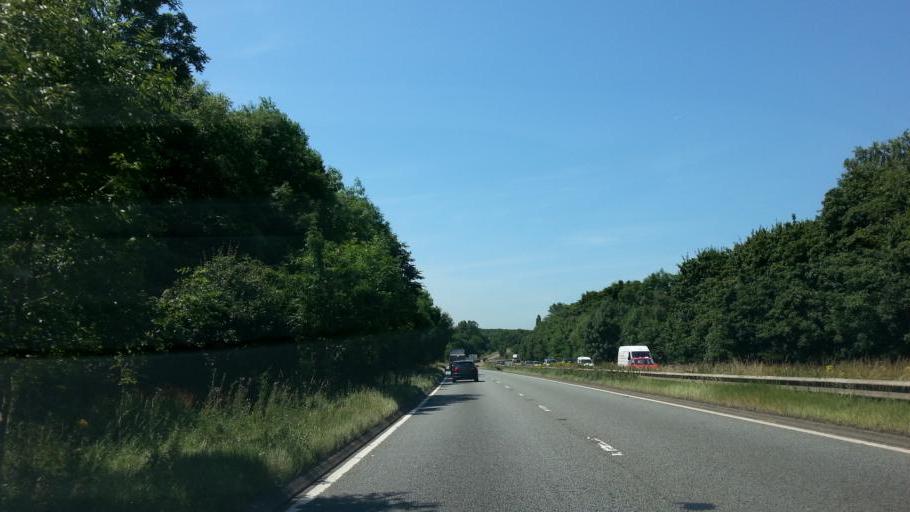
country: GB
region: England
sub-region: Derbyshire
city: Alfreton
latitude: 53.0904
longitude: -1.3860
